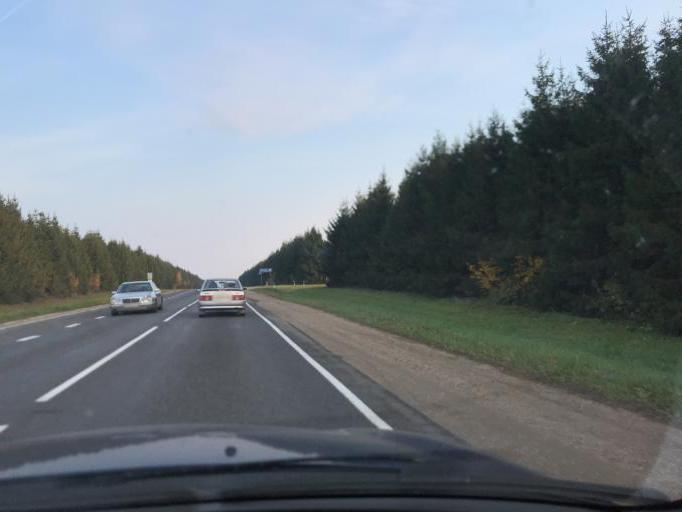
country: BY
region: Grodnenskaya
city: Karelichy
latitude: 53.5923
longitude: 26.0820
